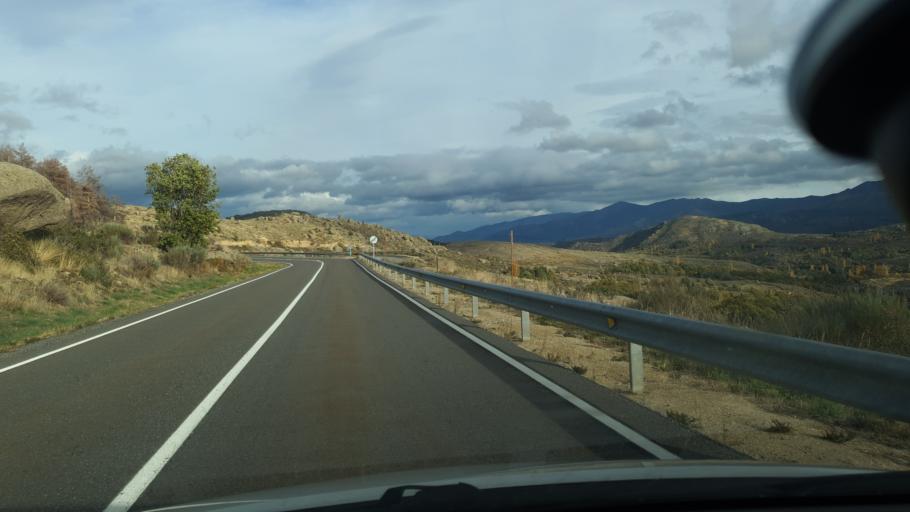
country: ES
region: Castille and Leon
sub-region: Provincia de Avila
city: Hoyocasero
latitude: 40.3916
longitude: -4.9547
